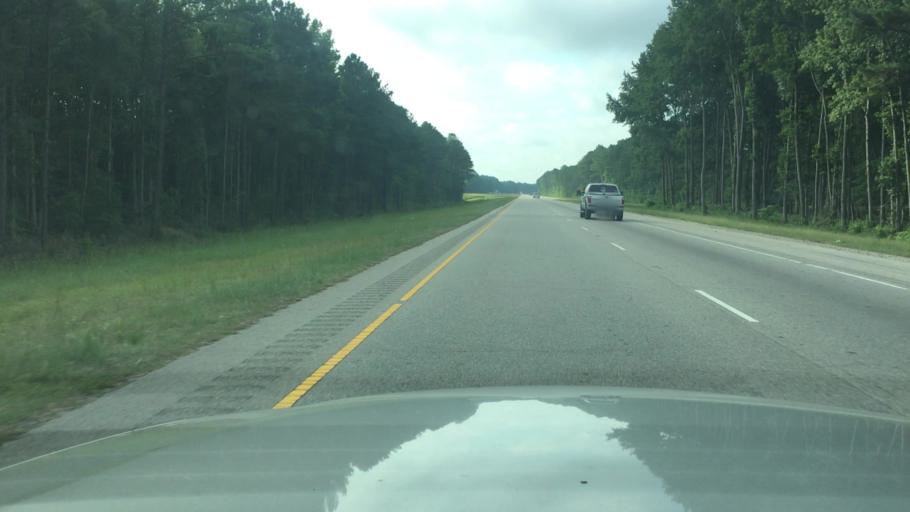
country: US
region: North Carolina
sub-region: Cumberland County
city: Fayetteville
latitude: 34.9750
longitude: -78.8558
